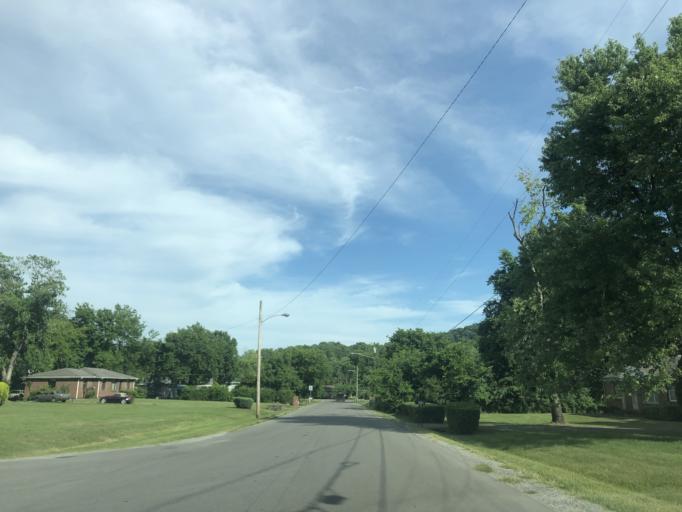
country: US
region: Tennessee
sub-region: Davidson County
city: Nashville
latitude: 36.2120
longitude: -86.8317
